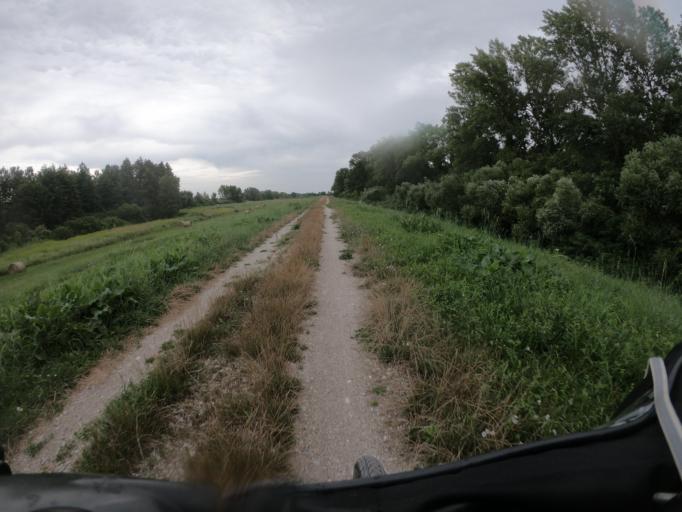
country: HU
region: Jasz-Nagykun-Szolnok
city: Tiszafured
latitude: 47.6827
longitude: 20.7788
